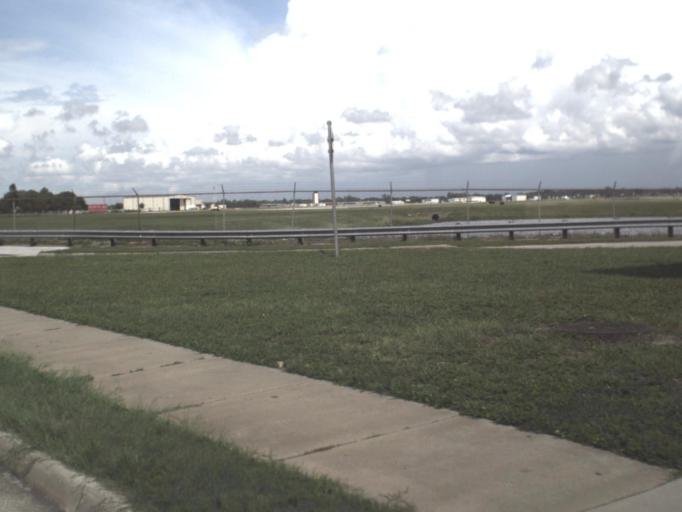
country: US
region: Florida
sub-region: Manatee County
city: Whitfield
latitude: 27.3868
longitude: -82.5584
